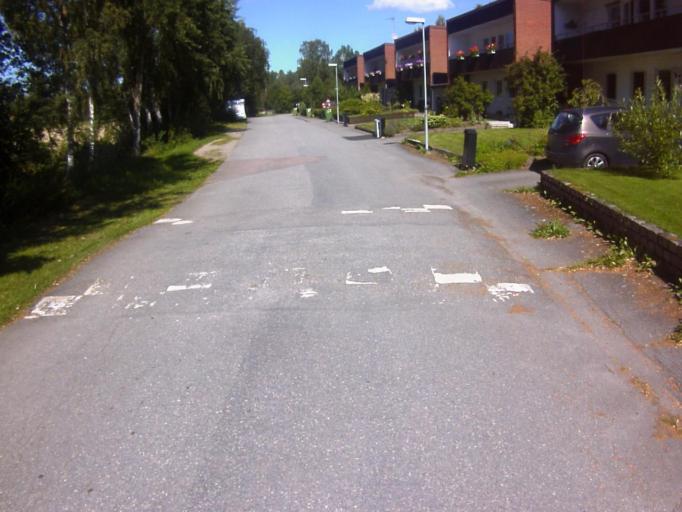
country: SE
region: Soedermanland
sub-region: Eskilstuna Kommun
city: Hallbybrunn
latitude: 59.3846
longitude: 16.4296
